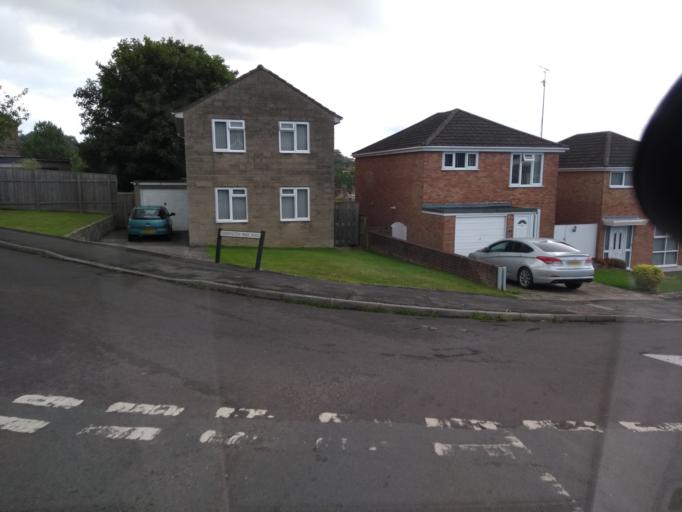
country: GB
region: England
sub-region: Somerset
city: Wincanton
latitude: 51.0564
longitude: -2.4173
